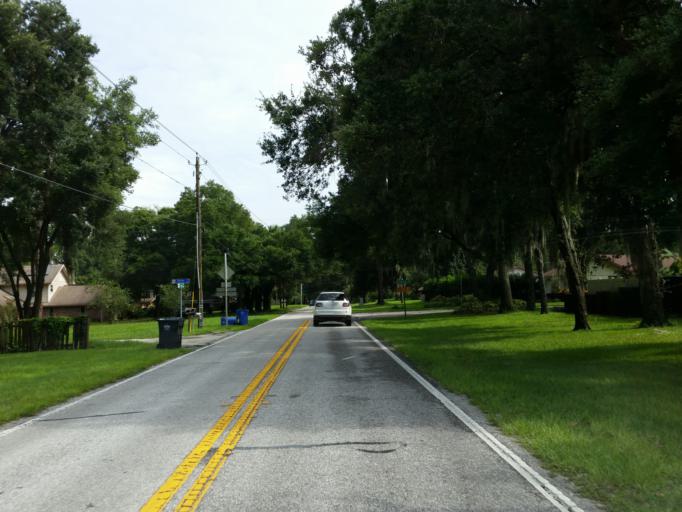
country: US
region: Florida
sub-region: Hillsborough County
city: Bloomingdale
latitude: 27.9092
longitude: -82.2528
